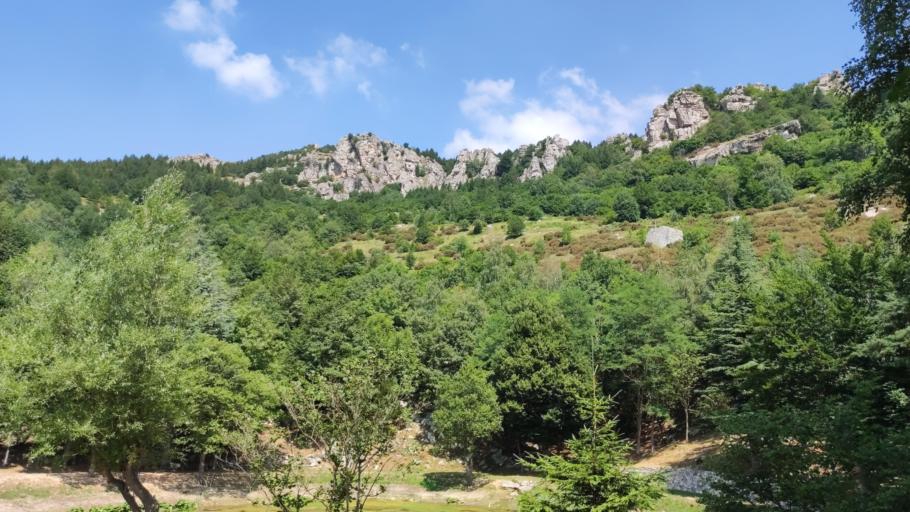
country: IT
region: Piedmont
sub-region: Provincia di Cuneo
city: Alto
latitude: 44.1187
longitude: 7.9932
